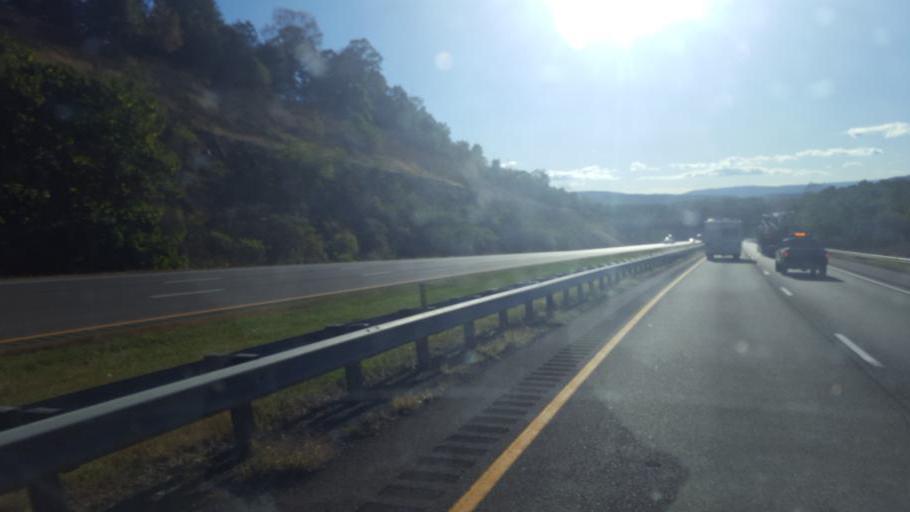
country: US
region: Maryland
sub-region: Allegany County
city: Cumberland
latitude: 39.6958
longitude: -78.5131
